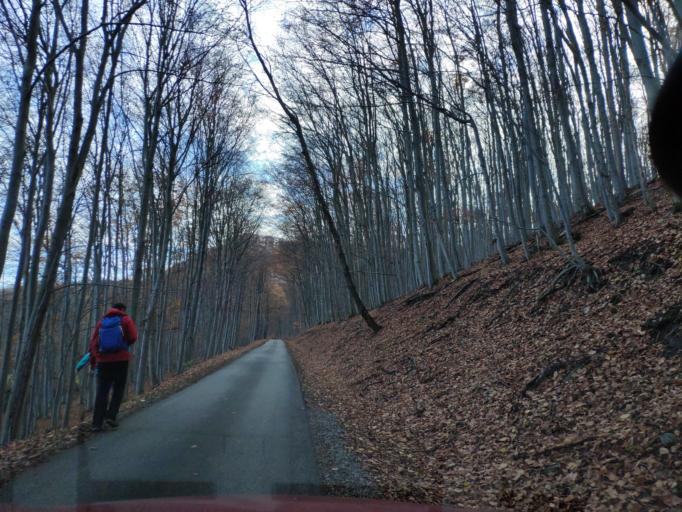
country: HU
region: Borsod-Abauj-Zemplen
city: Gonc
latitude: 48.5898
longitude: 21.4609
